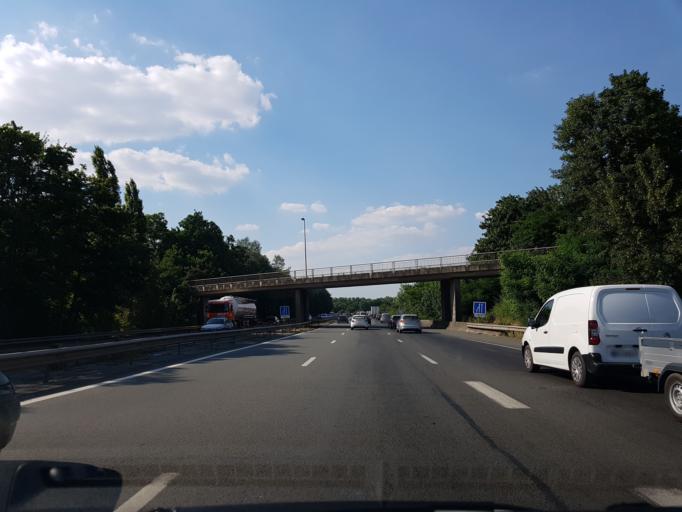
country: FR
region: Nord-Pas-de-Calais
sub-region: Departement du Pas-de-Calais
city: Courcelles-les-Lens
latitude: 50.4151
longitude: 3.0319
